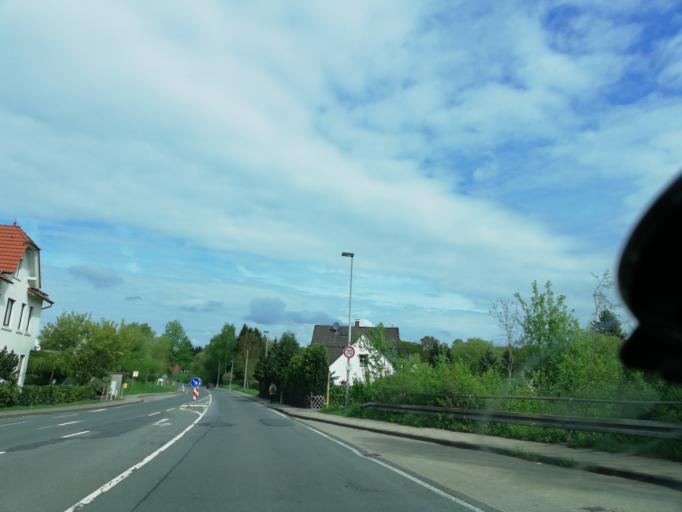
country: DE
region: North Rhine-Westphalia
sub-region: Regierungsbezirk Arnsberg
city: Schwelm
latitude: 51.3234
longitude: 7.2879
